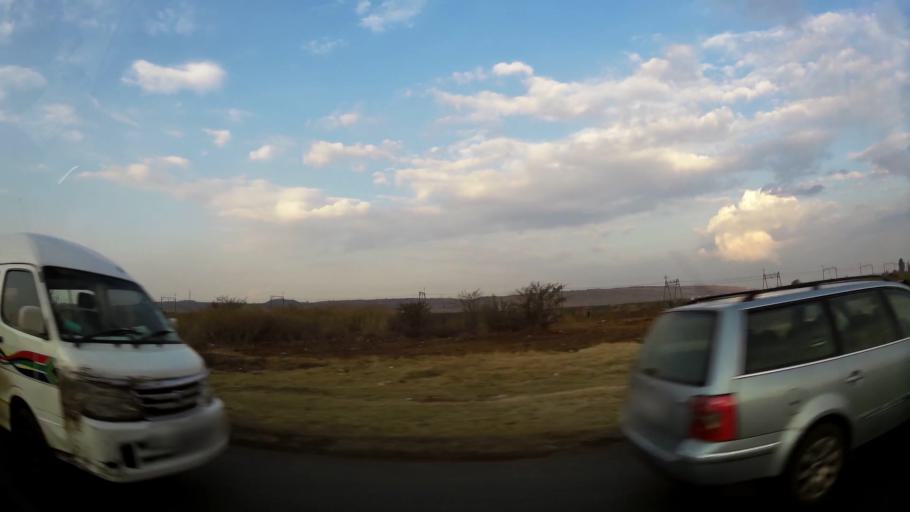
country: ZA
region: Gauteng
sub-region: City of Johannesburg Metropolitan Municipality
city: Orange Farm
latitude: -26.5921
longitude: 27.8508
